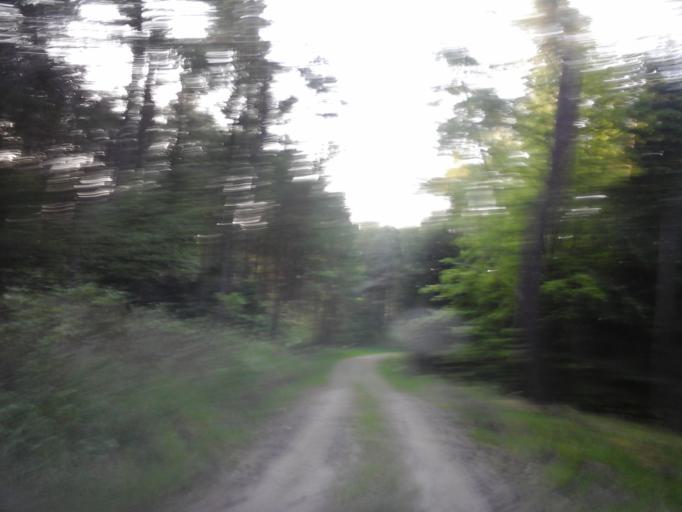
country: PL
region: West Pomeranian Voivodeship
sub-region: Powiat choszczenski
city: Krzecin
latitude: 53.0087
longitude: 15.5404
